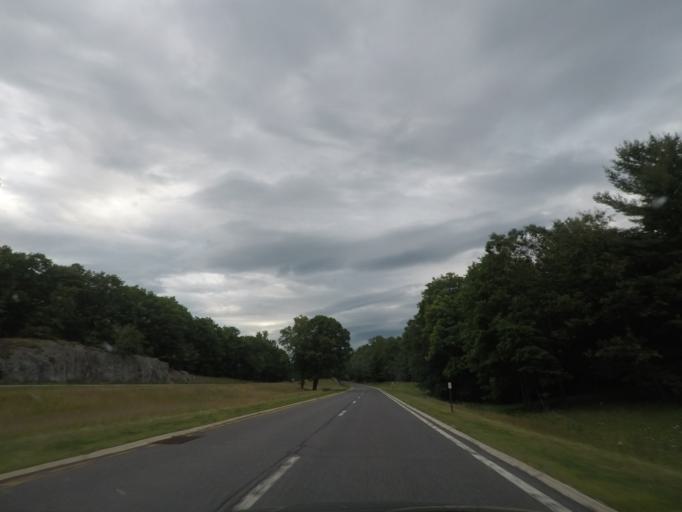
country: US
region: New York
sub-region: Dutchess County
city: Pine Plains
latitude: 42.0376
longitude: -73.7337
